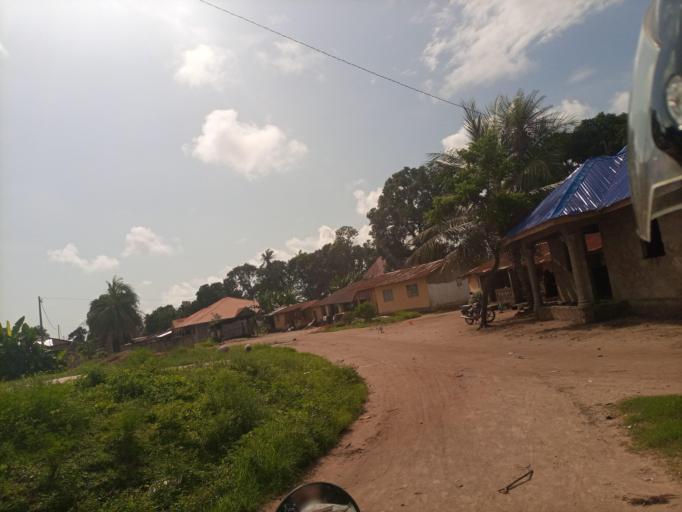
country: SL
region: Northern Province
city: Masoyila
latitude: 8.6102
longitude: -13.1724
